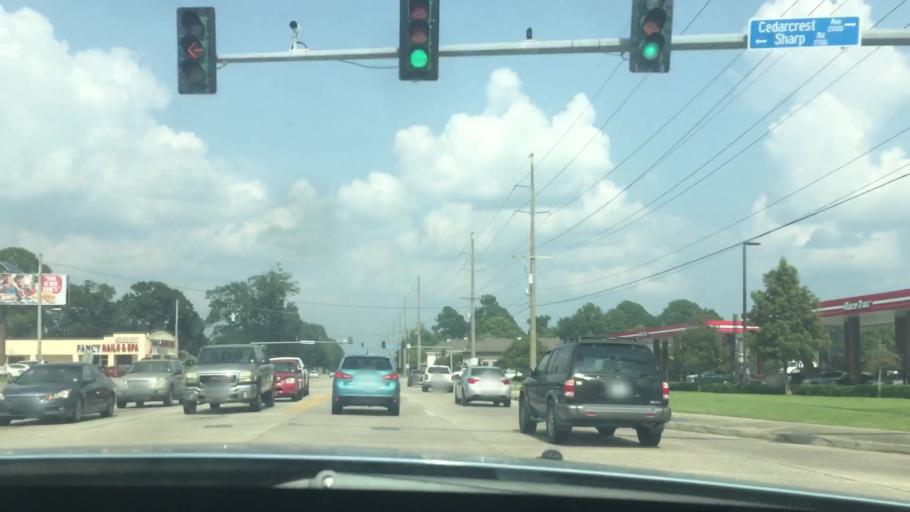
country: US
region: Louisiana
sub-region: East Baton Rouge Parish
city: Westminster
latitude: 30.4341
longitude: -91.0676
